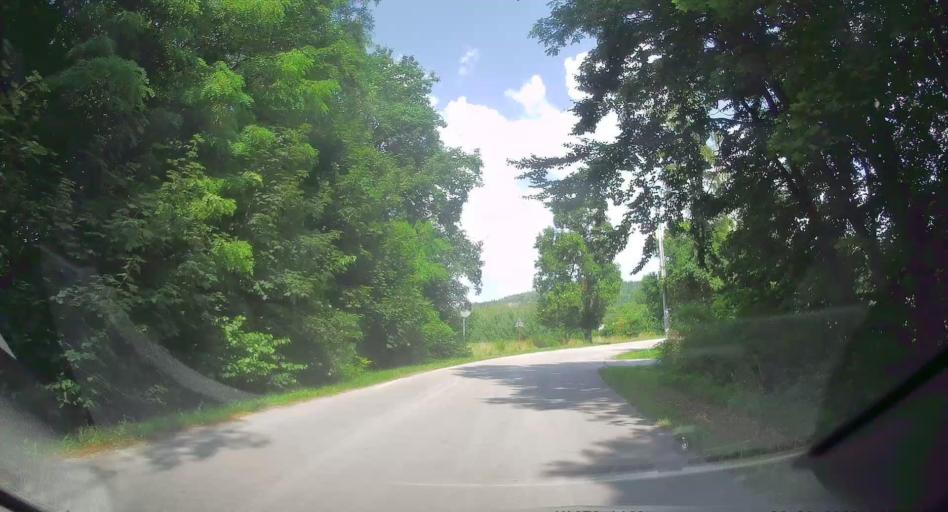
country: PL
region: Swietokrzyskie
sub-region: Powiat kielecki
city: Checiny
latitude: 50.7905
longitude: 20.4508
